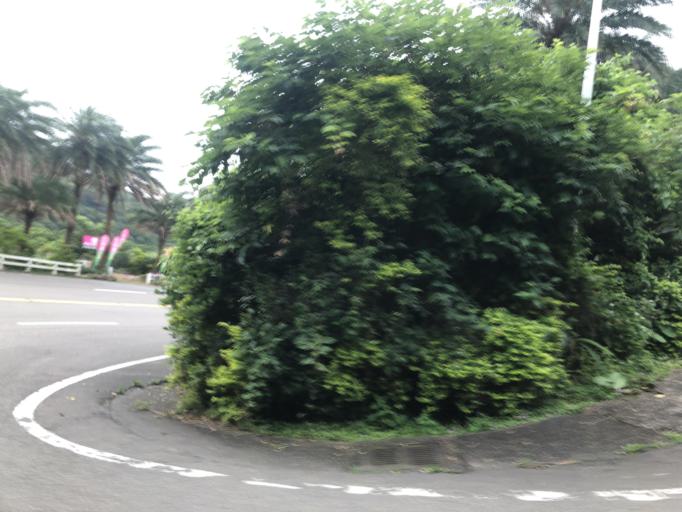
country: TW
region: Taiwan
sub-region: Keelung
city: Keelung
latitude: 25.2007
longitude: 121.6827
